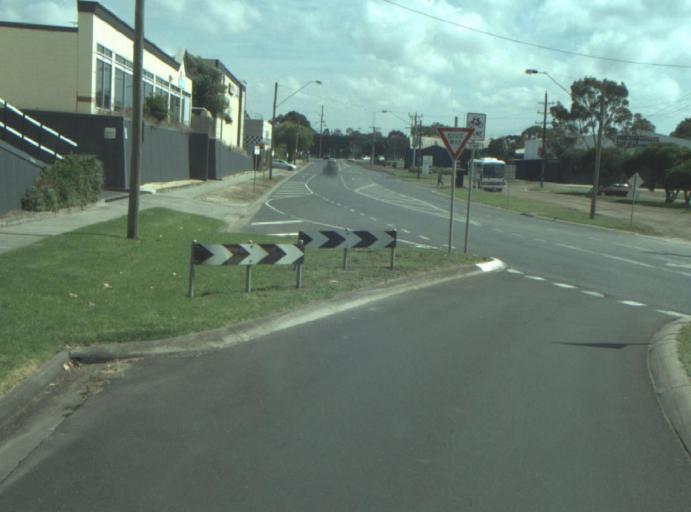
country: AU
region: Victoria
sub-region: Greater Geelong
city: Breakwater
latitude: -38.1708
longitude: 144.3502
